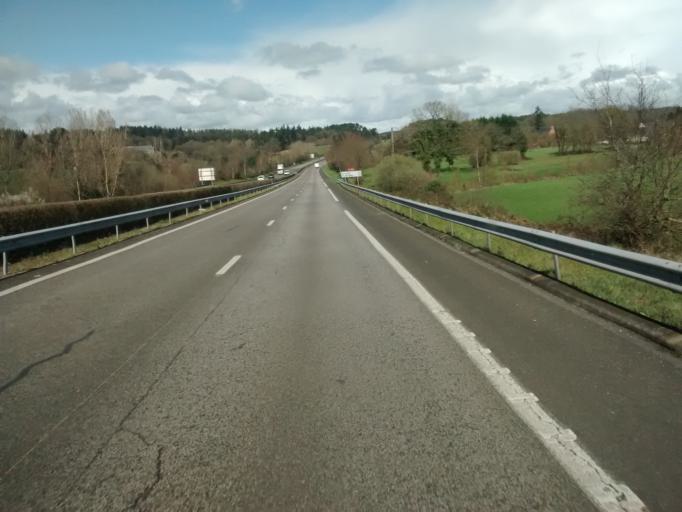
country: FR
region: Brittany
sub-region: Departement du Morbihan
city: Molac
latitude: 47.7882
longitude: -2.4547
